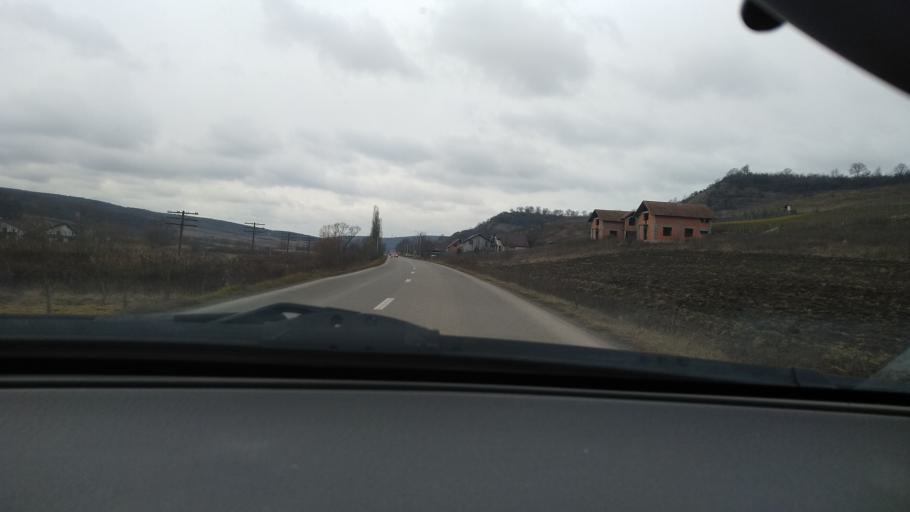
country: RO
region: Mures
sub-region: Comuna Livezeni
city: Livezeni
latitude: 46.5441
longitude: 24.6652
